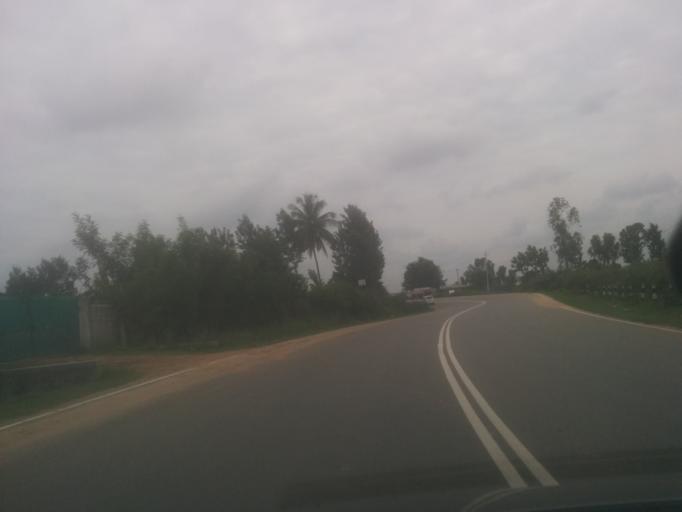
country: IN
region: Karnataka
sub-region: Hassan
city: Belur
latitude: 13.1652
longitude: 75.8819
